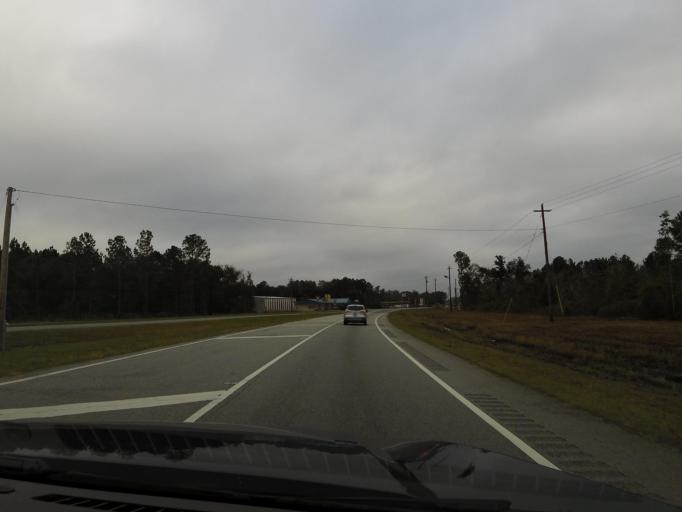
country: US
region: Georgia
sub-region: Charlton County
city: Folkston
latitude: 30.8625
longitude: -82.0120
